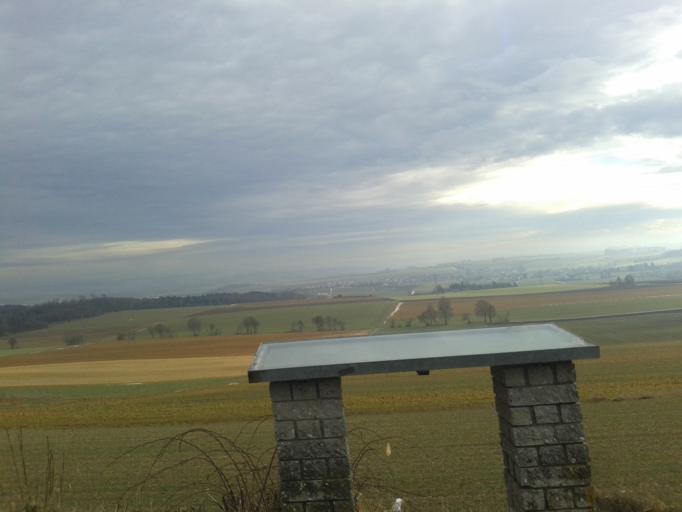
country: DE
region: Baden-Wuerttemberg
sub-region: Tuebingen Region
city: Erbach
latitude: 48.3766
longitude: 9.8976
